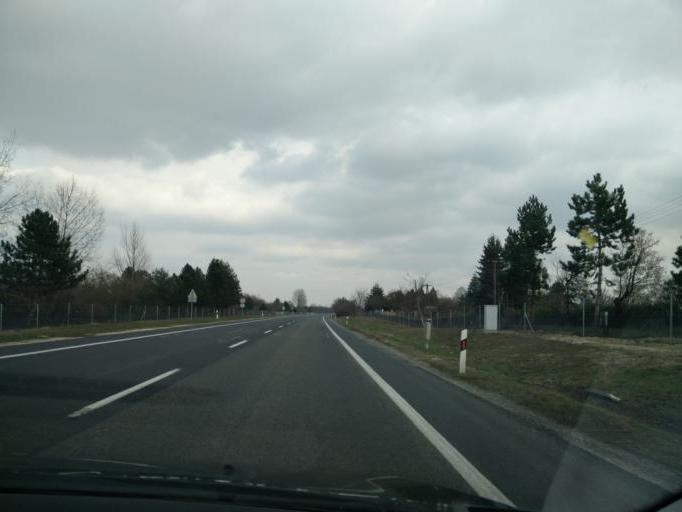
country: HU
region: Gyor-Moson-Sopron
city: Gyor
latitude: 47.7161
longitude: 17.7169
